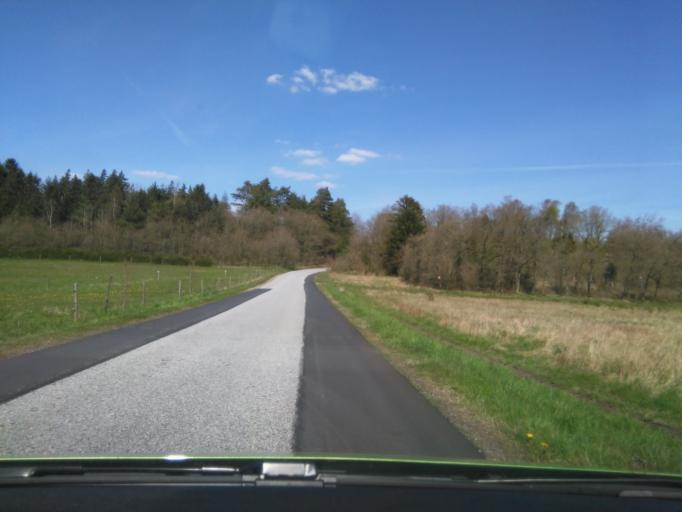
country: DK
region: Central Jutland
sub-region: Viborg Kommune
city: Viborg
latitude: 56.3762
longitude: 9.2945
